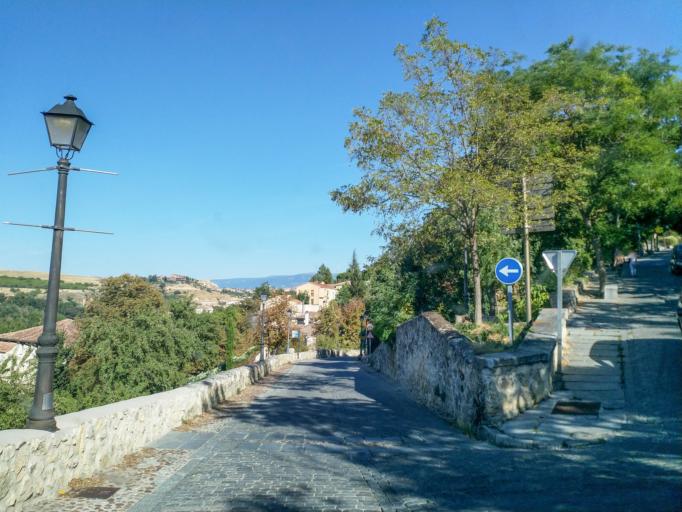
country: ES
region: Castille and Leon
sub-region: Provincia de Segovia
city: Segovia
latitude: 40.9530
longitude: -4.1285
